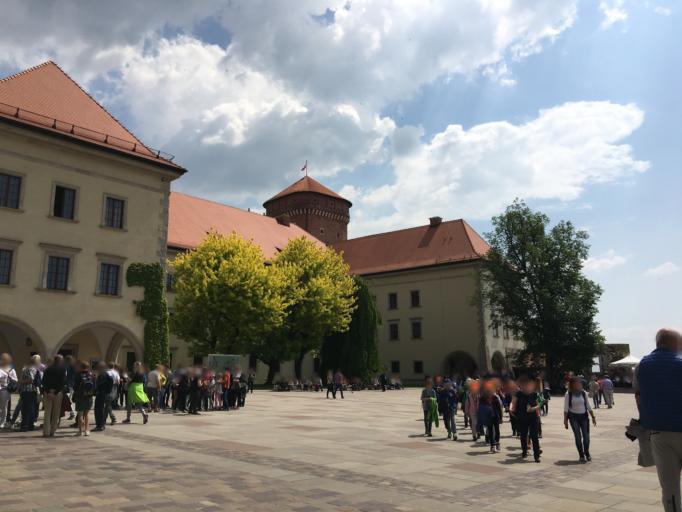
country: PL
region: Lesser Poland Voivodeship
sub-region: Krakow
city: Krakow
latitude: 50.0543
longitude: 19.9351
